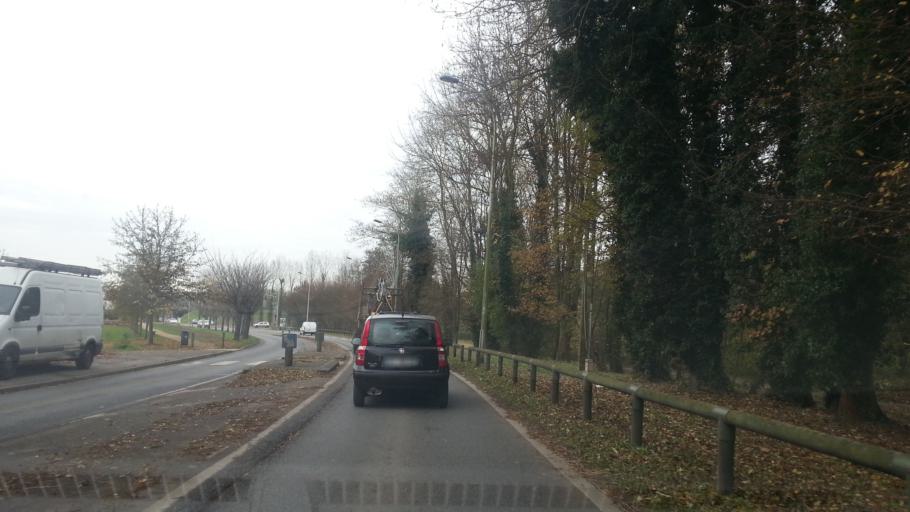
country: FR
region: Picardie
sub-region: Departement de l'Oise
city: Thiverny
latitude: 49.2543
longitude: 2.4408
